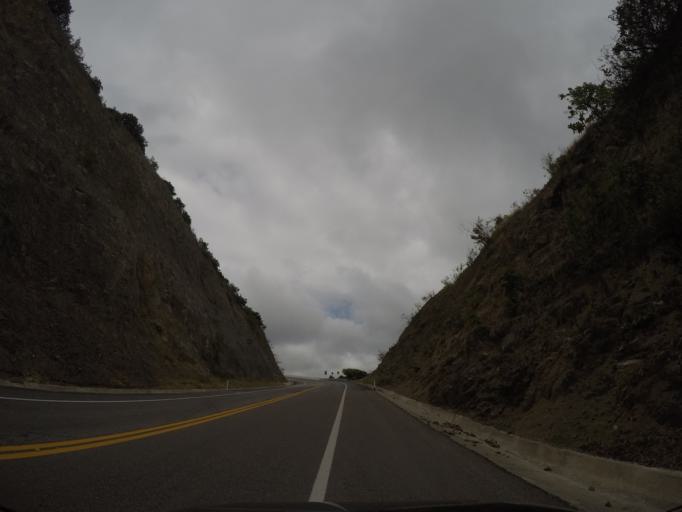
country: MX
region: Oaxaca
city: San Lorenzo Albarradas
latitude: 16.9339
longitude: -96.2666
